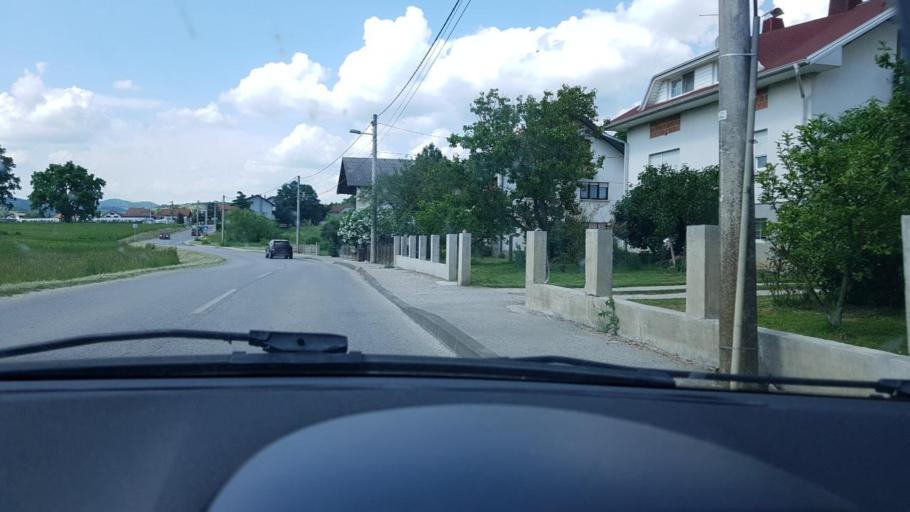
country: HR
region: Grad Zagreb
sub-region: Sesvete
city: Sesvete
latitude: 45.8959
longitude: 16.1675
